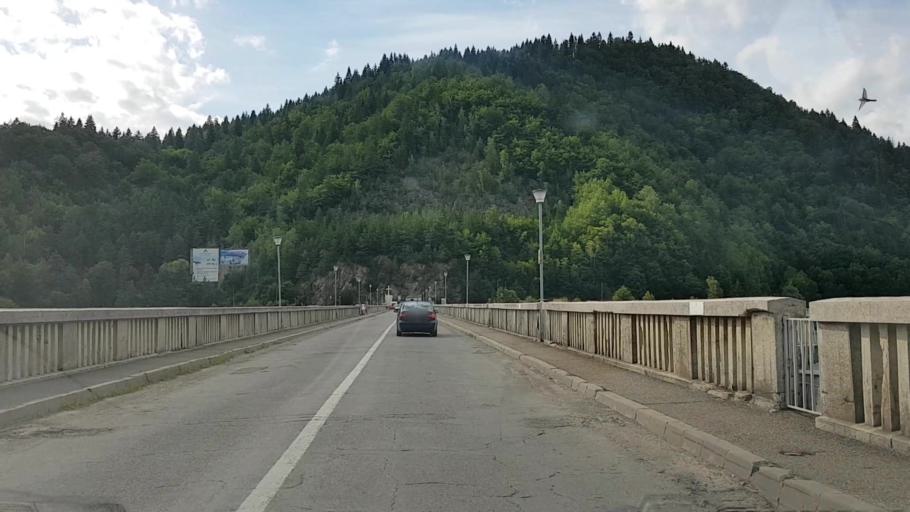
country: RO
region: Neamt
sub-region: Comuna Bicaz
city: Dodeni
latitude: 46.9381
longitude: 26.1036
